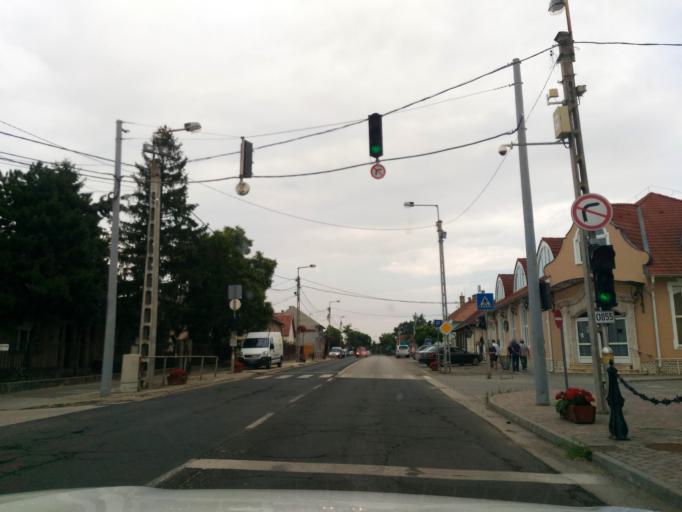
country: HU
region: Pest
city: Alsonemedi
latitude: 47.3125
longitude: 19.1677
